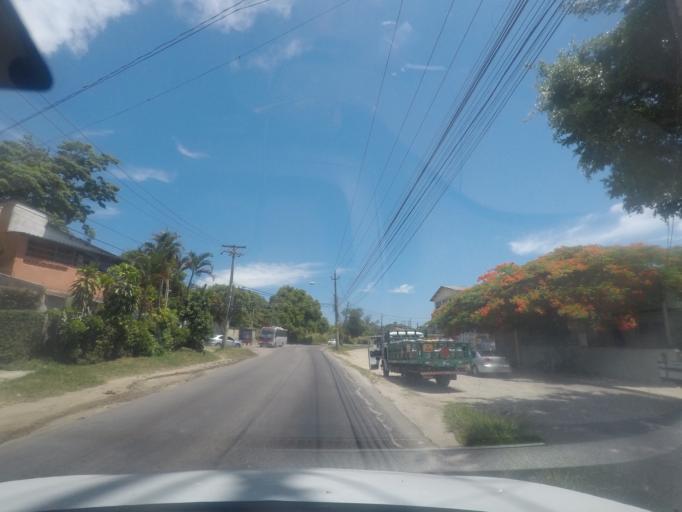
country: BR
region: Rio de Janeiro
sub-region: Itaguai
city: Itaguai
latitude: -22.9956
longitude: -43.6502
